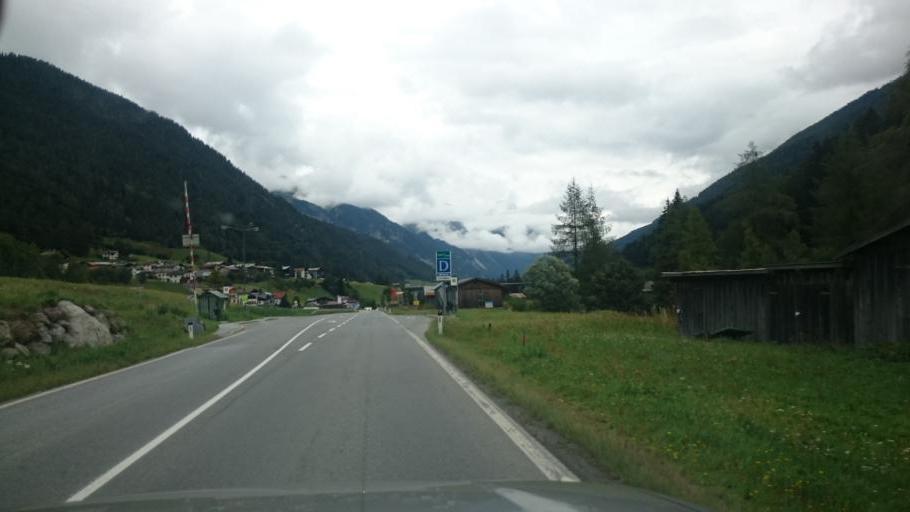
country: AT
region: Tyrol
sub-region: Politischer Bezirk Landeck
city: Sankt Anton am Arlberg
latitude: 47.1393
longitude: 10.2868
